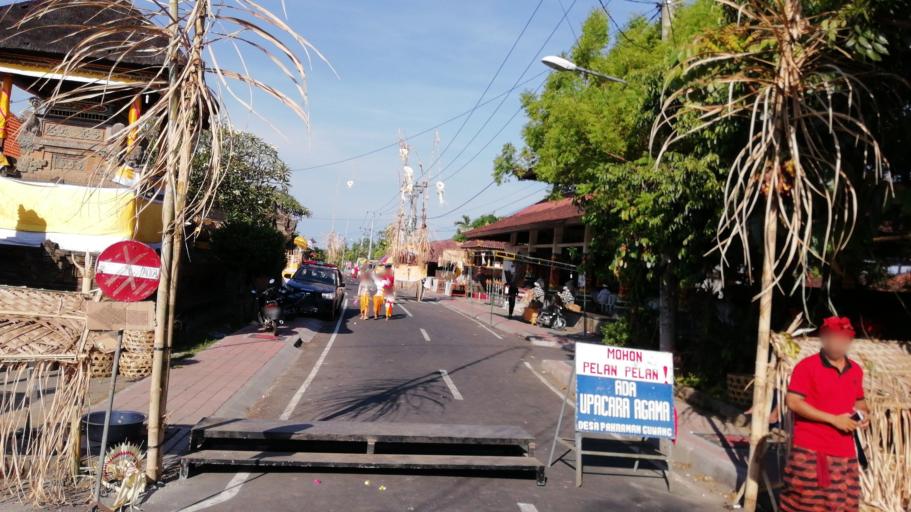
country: ID
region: Bali
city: Banjar Pasekan
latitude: -8.6107
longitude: 115.2851
